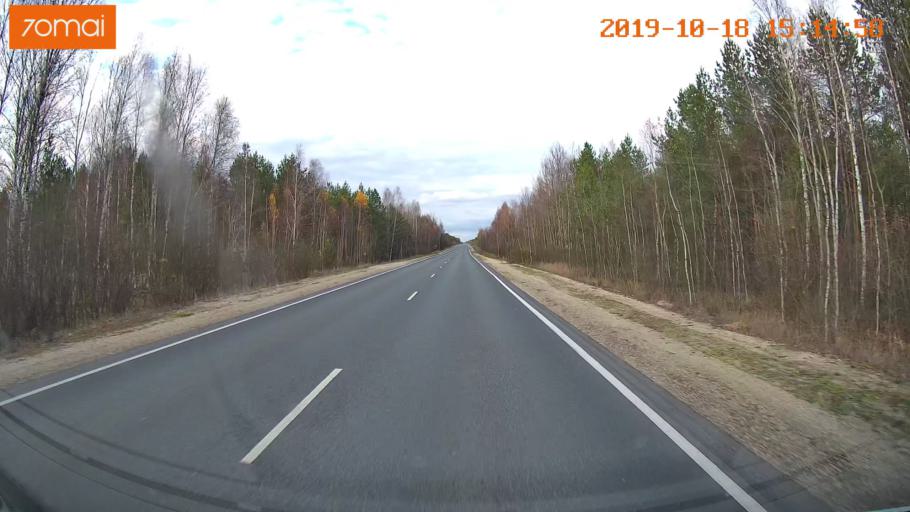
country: RU
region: Vladimir
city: Gus'-Khrustal'nyy
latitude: 55.6111
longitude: 40.7214
